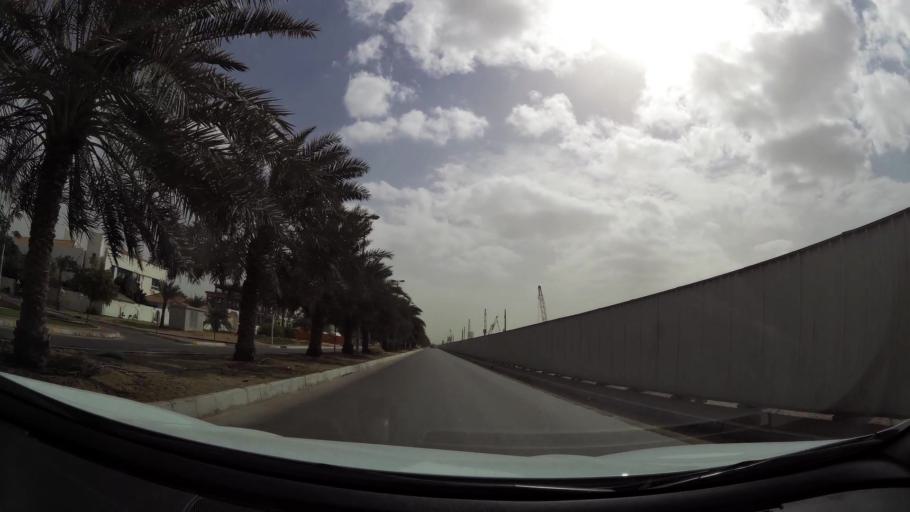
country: AE
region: Abu Dhabi
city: Abu Dhabi
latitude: 24.4038
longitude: 54.4957
